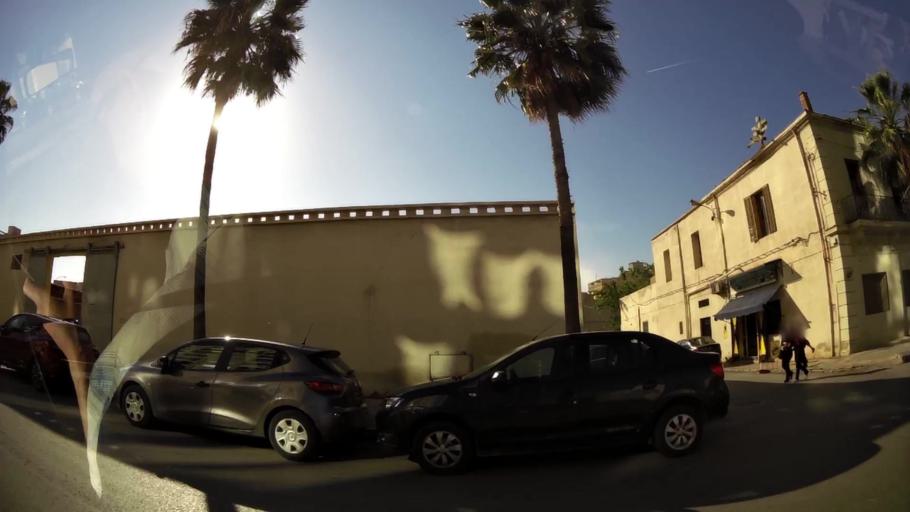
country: MA
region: Oriental
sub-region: Oujda-Angad
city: Oujda
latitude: 34.6857
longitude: -1.9136
